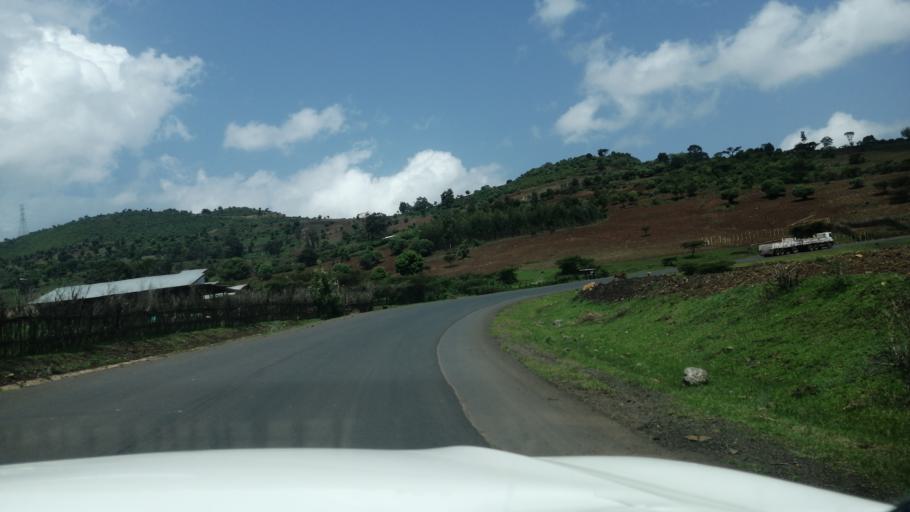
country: ET
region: Oromiya
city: Gedo
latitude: 8.9784
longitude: 37.6018
